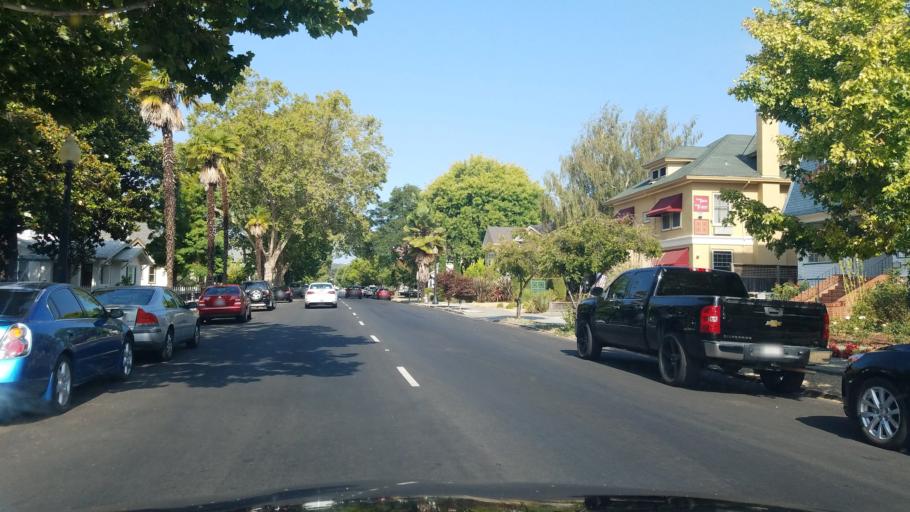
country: US
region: California
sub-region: Napa County
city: Napa
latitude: 38.2975
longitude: -122.2945
